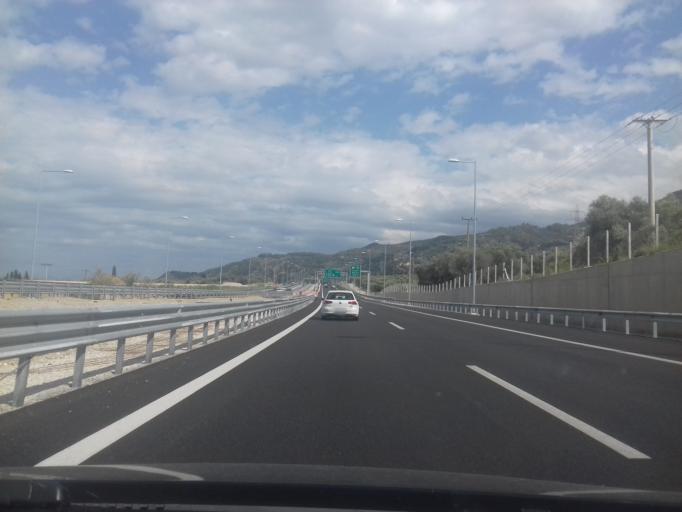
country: GR
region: West Greece
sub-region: Nomos Achaias
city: Aiyira
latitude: 38.1343
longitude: 22.3903
